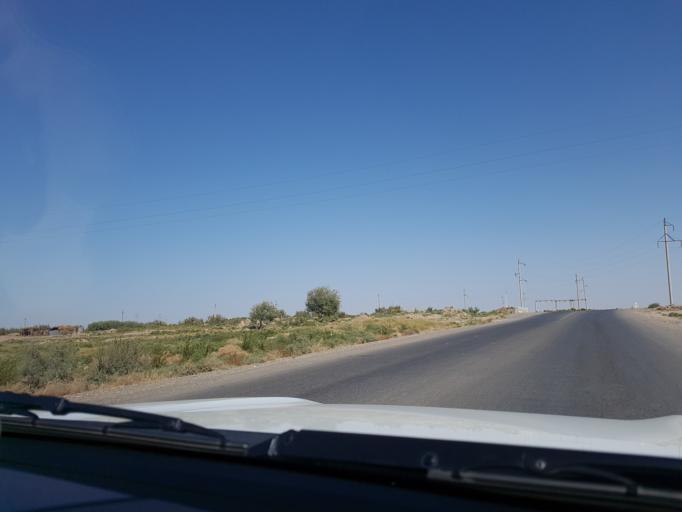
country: IR
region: Razavi Khorasan
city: Sarakhs
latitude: 36.5240
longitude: 61.2351
